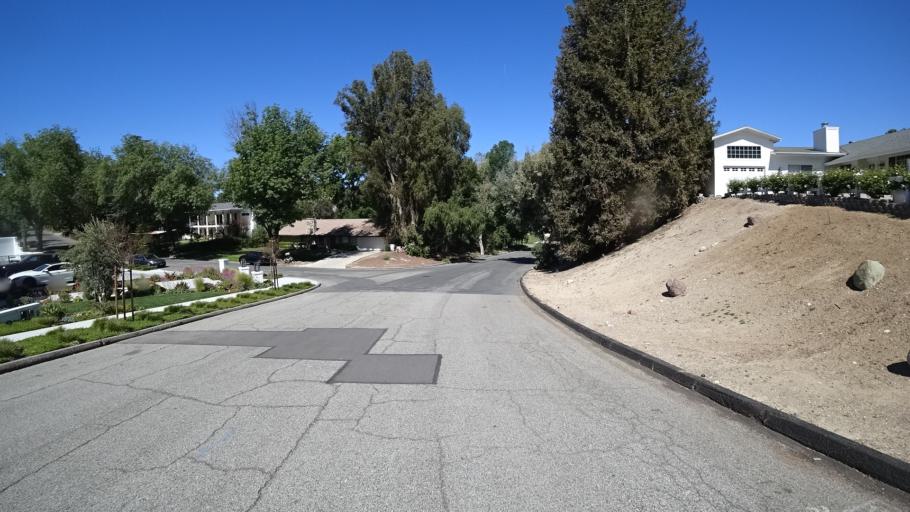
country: US
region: California
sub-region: Ventura County
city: Thousand Oaks
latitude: 34.1899
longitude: -118.8491
